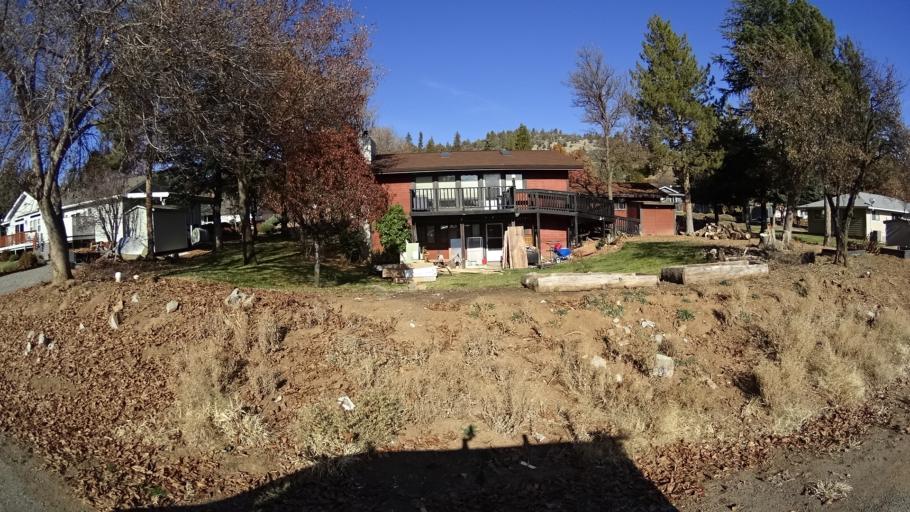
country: US
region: California
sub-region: Siskiyou County
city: Yreka
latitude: 41.6919
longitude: -122.6520
